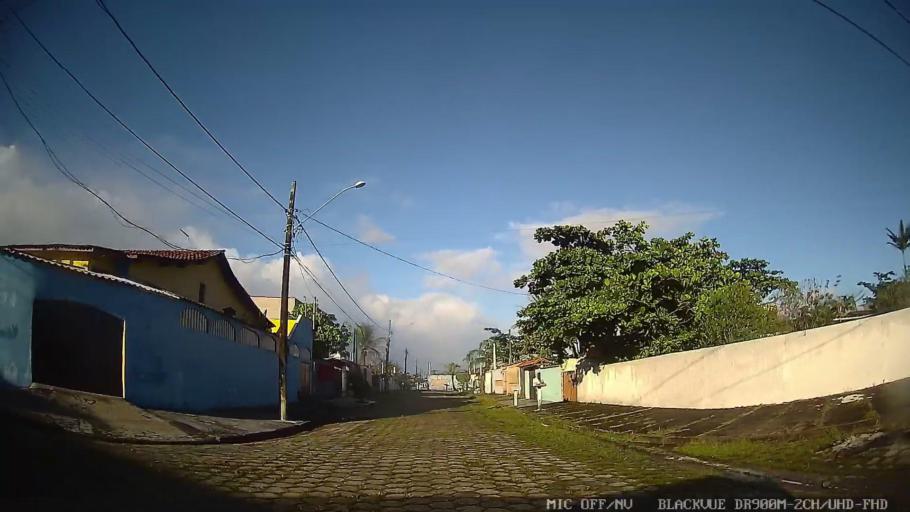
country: BR
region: Sao Paulo
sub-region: Itanhaem
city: Itanhaem
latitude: -24.2429
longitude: -46.8878
